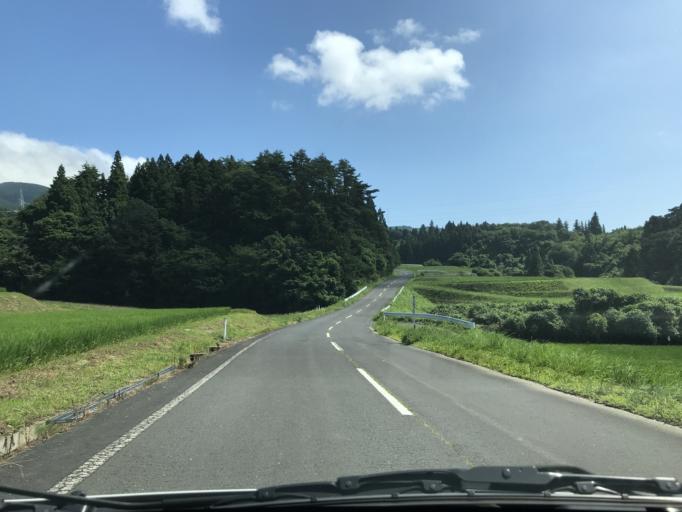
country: JP
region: Iwate
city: Ofunato
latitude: 39.0051
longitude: 141.4251
